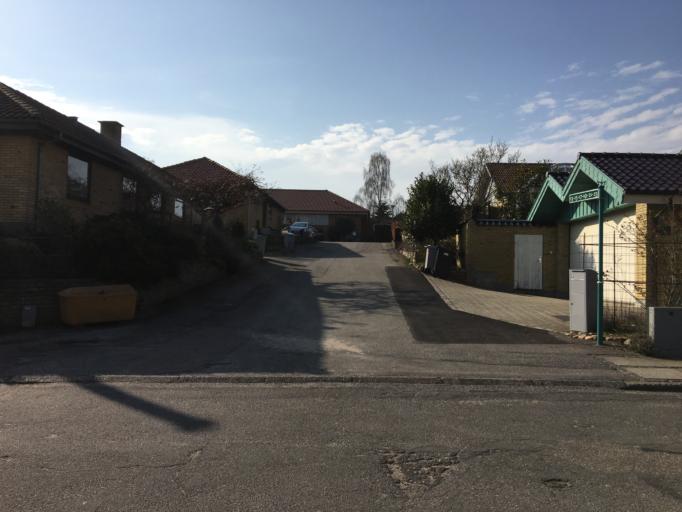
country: DK
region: South Denmark
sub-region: Middelfart Kommune
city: Middelfart
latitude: 55.5044
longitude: 9.7131
